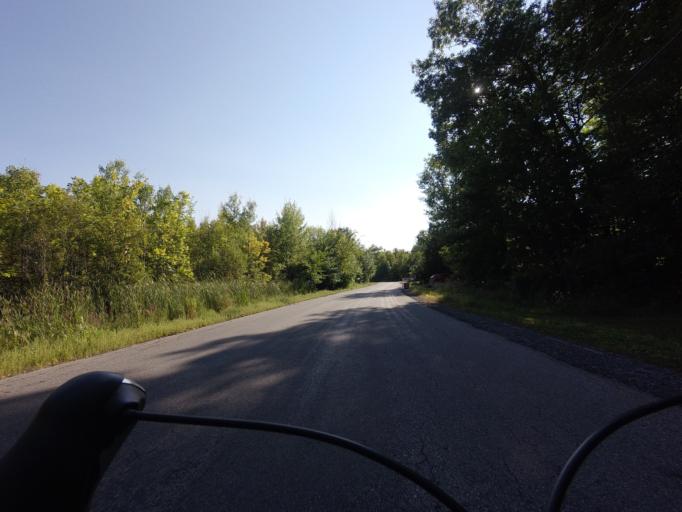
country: CA
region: Ontario
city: Bells Corners
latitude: 45.4856
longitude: -76.0486
